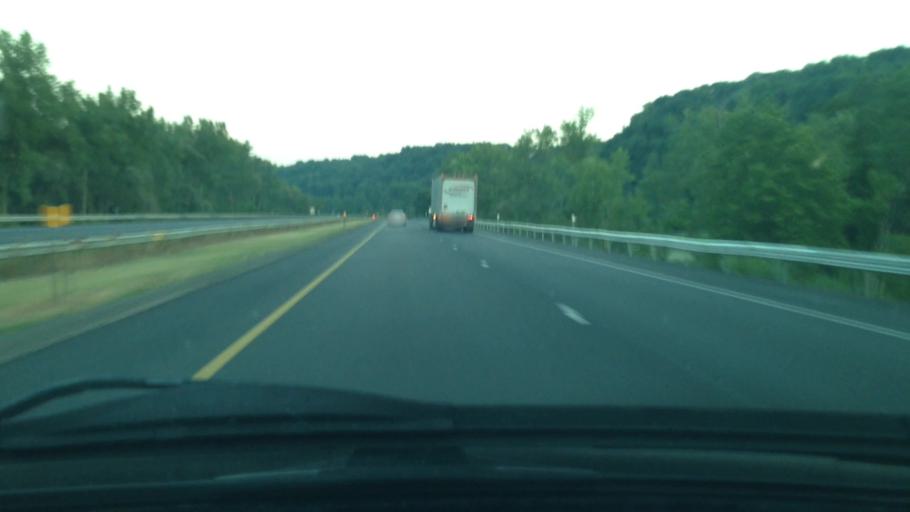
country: US
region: New York
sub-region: Montgomery County
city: Fort Plain
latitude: 42.9236
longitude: -74.6136
